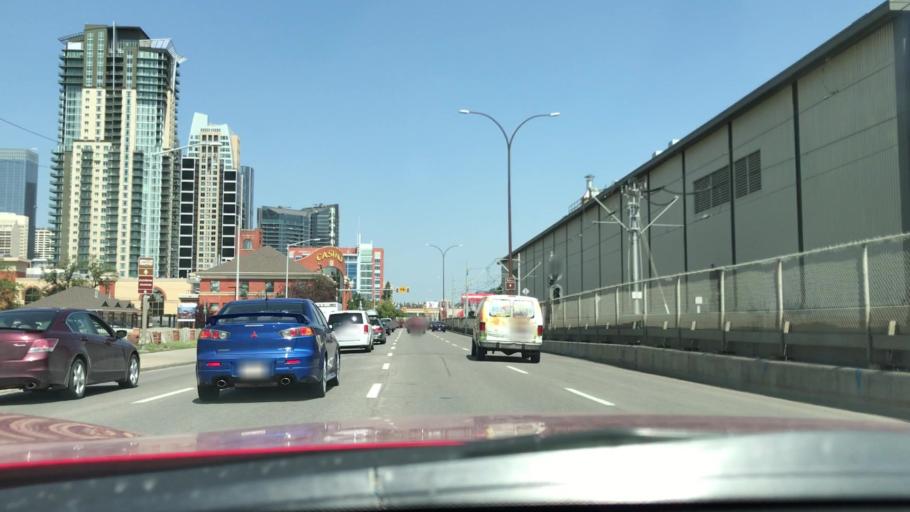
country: CA
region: Alberta
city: Calgary
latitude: 51.0355
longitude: -114.0589
